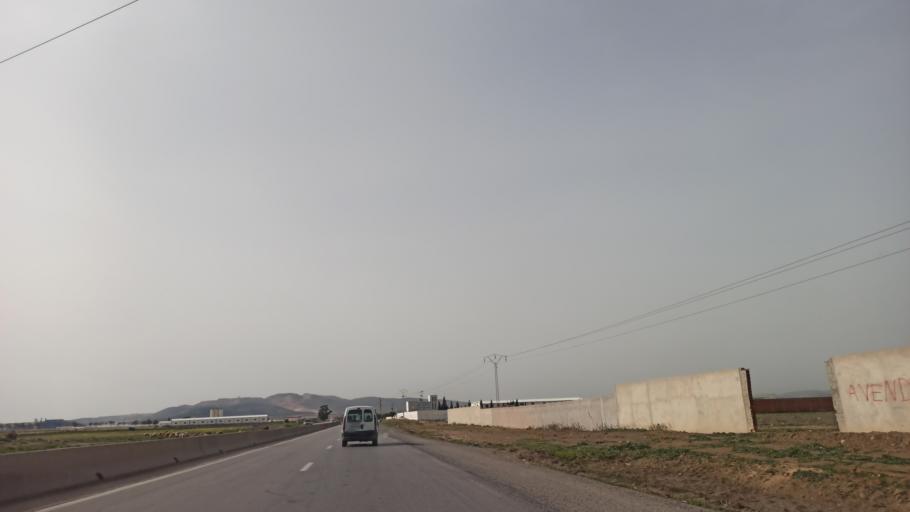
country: TN
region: Tunis
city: La Mohammedia
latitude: 36.5723
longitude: 10.0877
